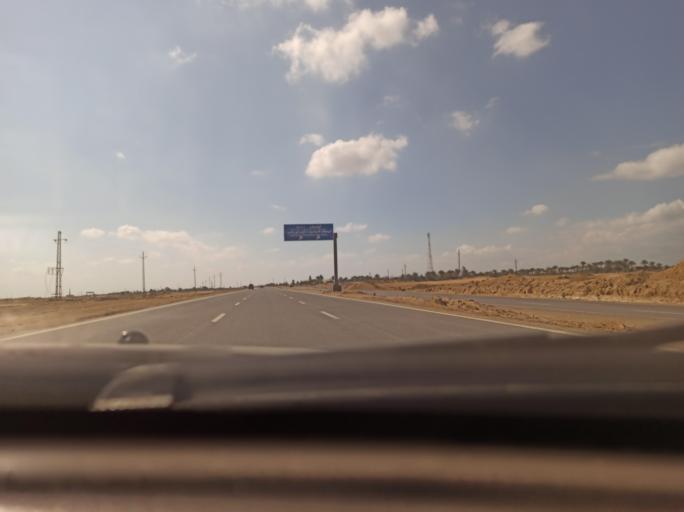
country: EG
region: Muhafazat al Fayyum
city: Al Wasitah
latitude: 29.3728
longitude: 31.0836
